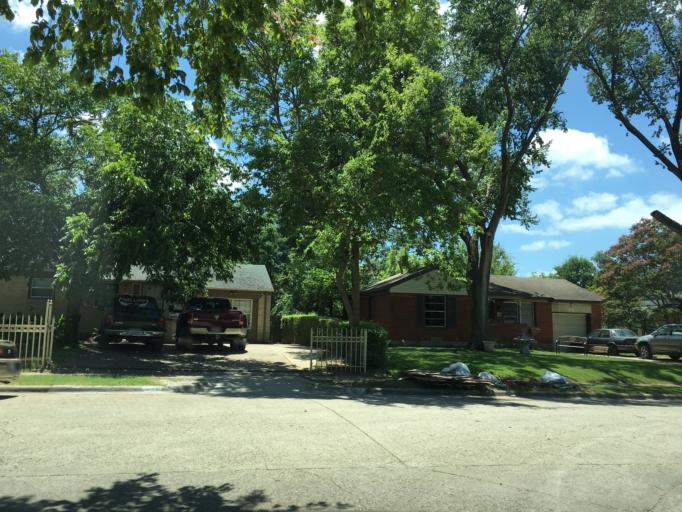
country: US
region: Texas
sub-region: Dallas County
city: Garland
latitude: 32.8440
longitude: -96.6710
